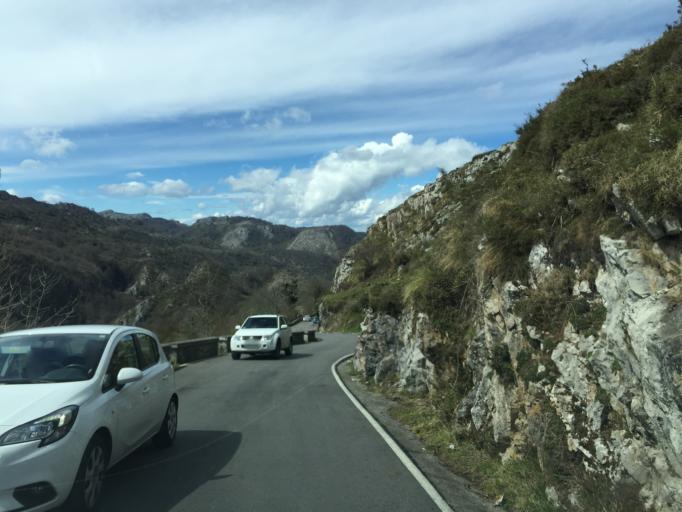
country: ES
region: Asturias
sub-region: Province of Asturias
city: Amieva
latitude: 43.2963
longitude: -5.0189
